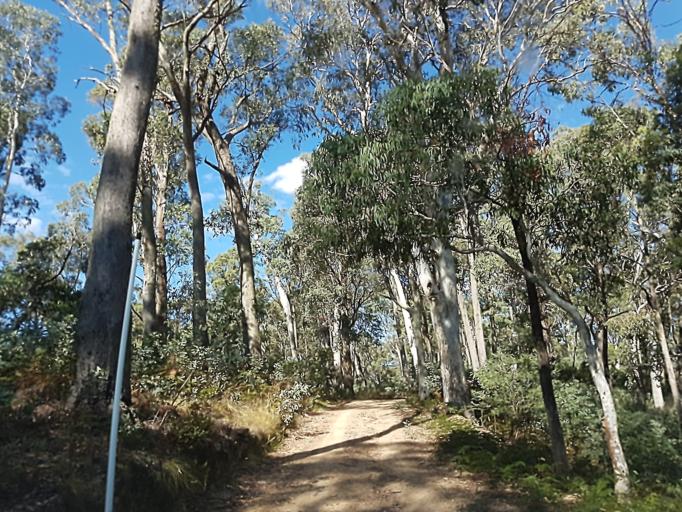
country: AU
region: Victoria
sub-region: Alpine
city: Mount Beauty
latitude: -36.9344
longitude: 147.0096
